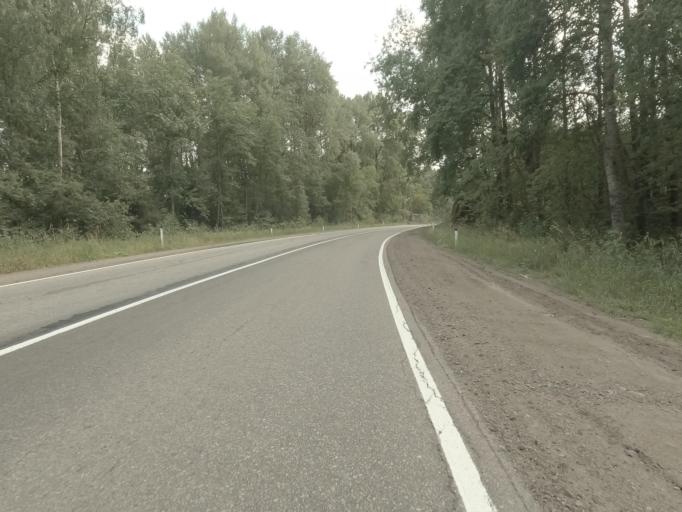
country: RU
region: Leningrad
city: Kamennogorsk
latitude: 60.8670
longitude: 28.9782
